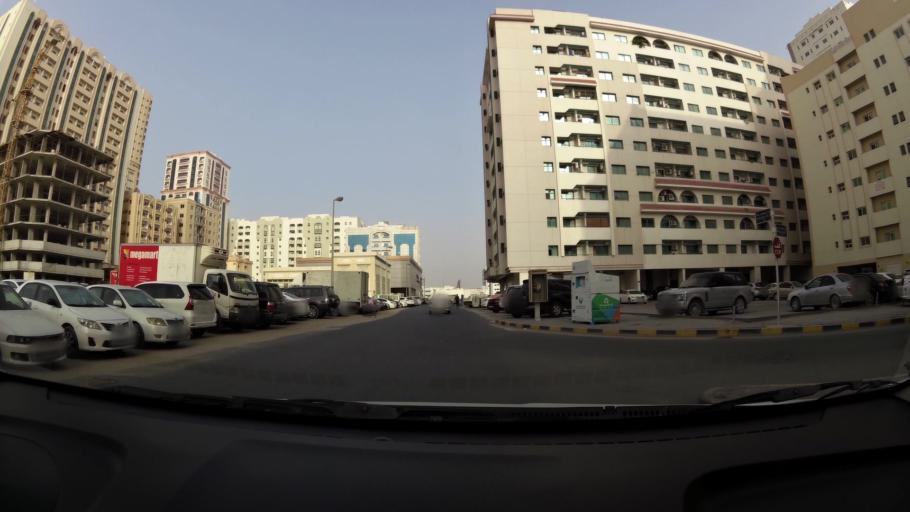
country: AE
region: Ash Shariqah
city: Sharjah
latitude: 25.3432
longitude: 55.4000
